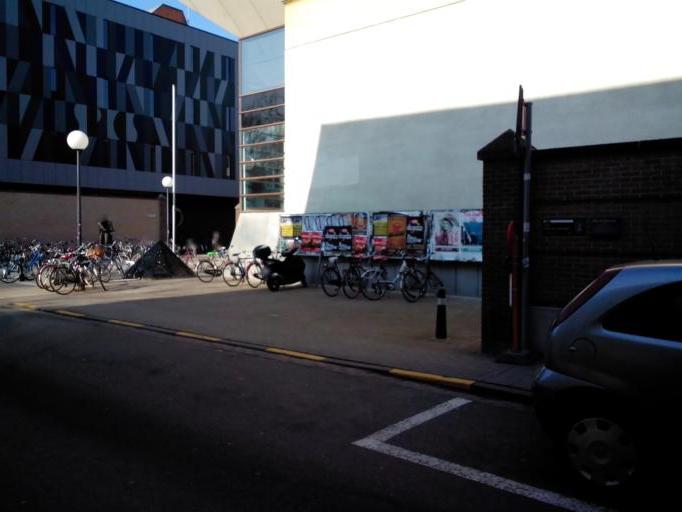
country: BE
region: Flanders
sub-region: Provincie Vlaams-Brabant
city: Leuven
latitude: 50.8762
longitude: 4.7033
